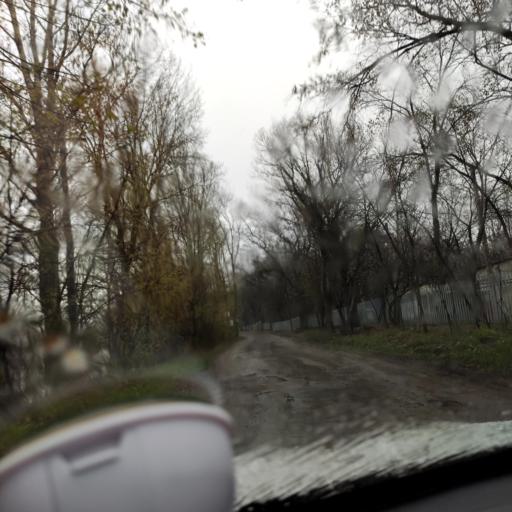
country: RU
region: Samara
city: Novokuybyshevsk
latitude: 53.1403
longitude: 49.9711
